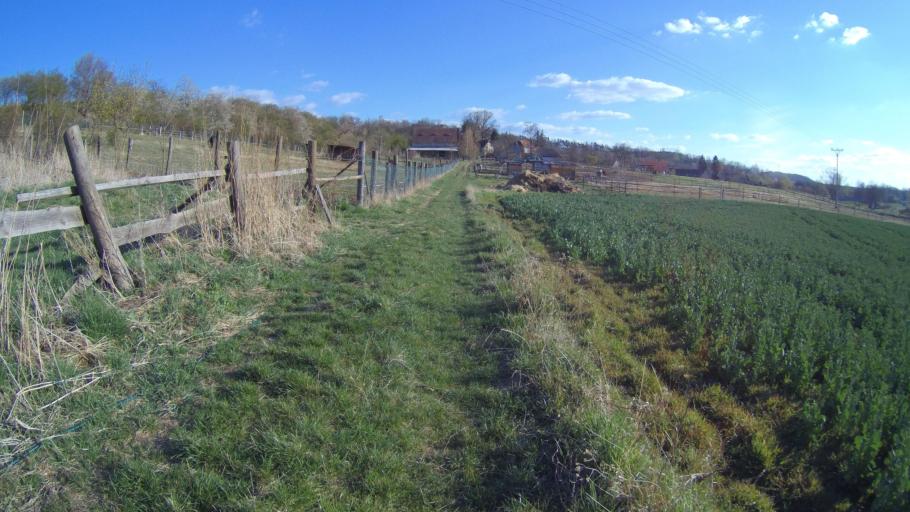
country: CZ
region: Ustecky
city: Zatec
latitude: 50.2932
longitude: 13.5766
